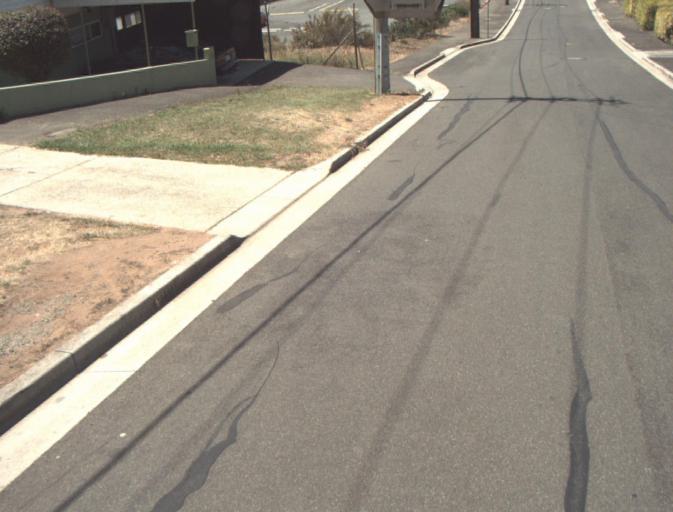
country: AU
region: Tasmania
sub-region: Launceston
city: West Launceston
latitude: -41.4570
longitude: 147.1402
